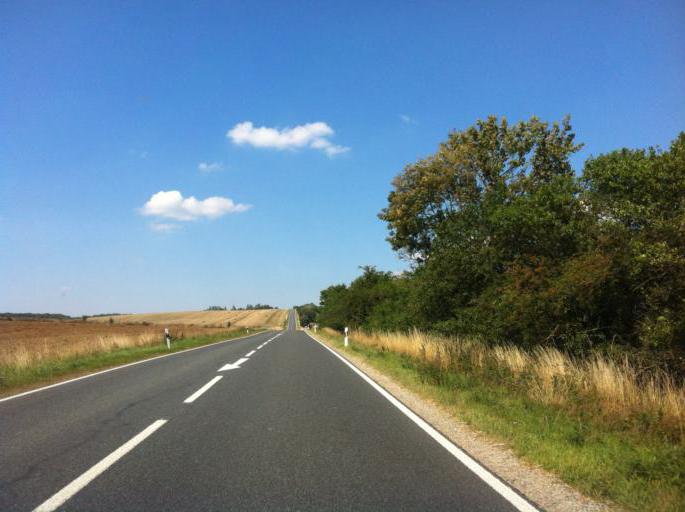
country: DE
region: Thuringia
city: Kefferhausen
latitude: 51.3248
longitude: 10.3001
